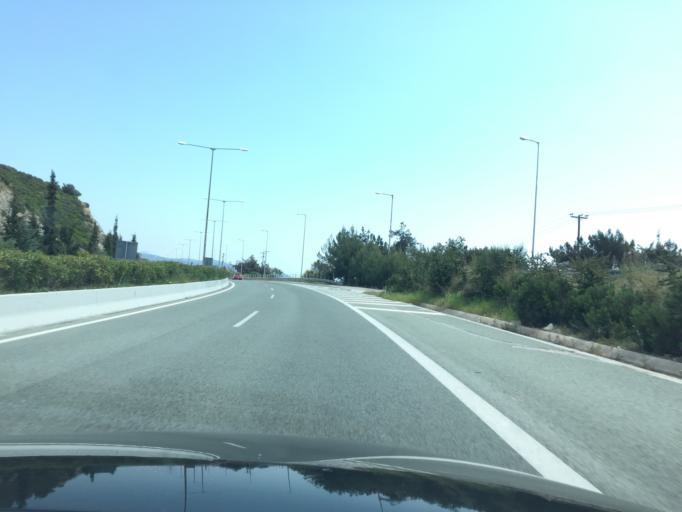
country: GR
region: Central Greece
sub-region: Nomos Fthiotidos
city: Pelasgia
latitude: 38.8911
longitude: 22.8314
